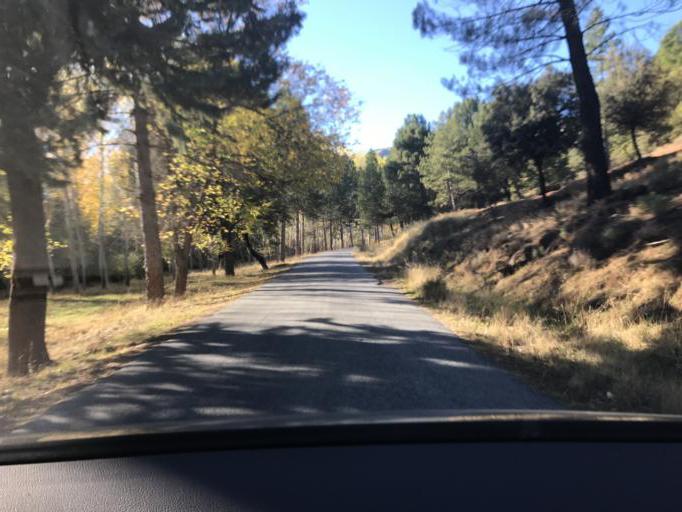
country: ES
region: Andalusia
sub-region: Provincia de Granada
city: Beas de Granada
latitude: 37.3052
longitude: -3.4610
